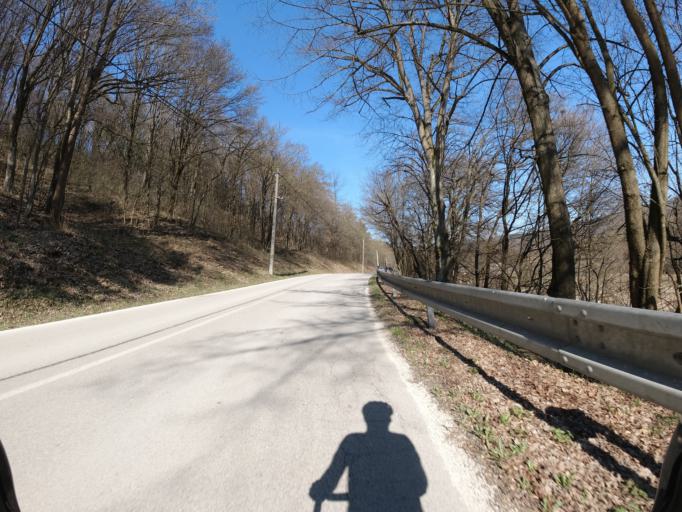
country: SK
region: Nitriansky
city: Stara Tura
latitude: 48.6989
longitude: 17.6980
